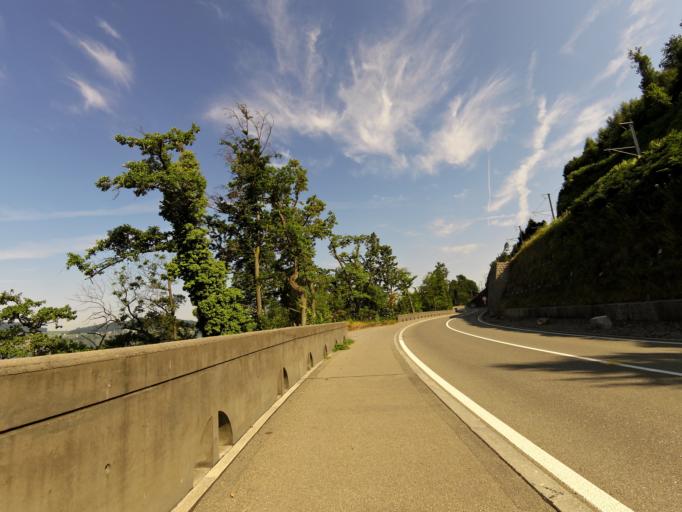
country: CH
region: Zug
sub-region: Zug
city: Walchwil
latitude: 47.1186
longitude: 8.4970
